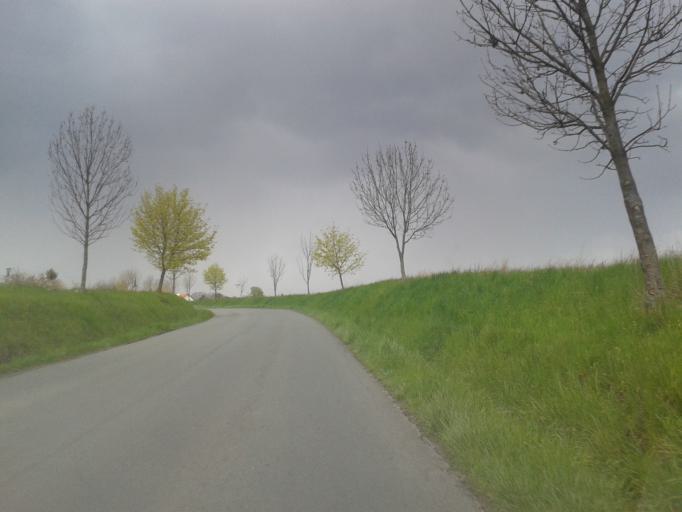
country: CZ
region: Central Bohemia
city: Hudlice
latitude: 49.9578
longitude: 13.9834
